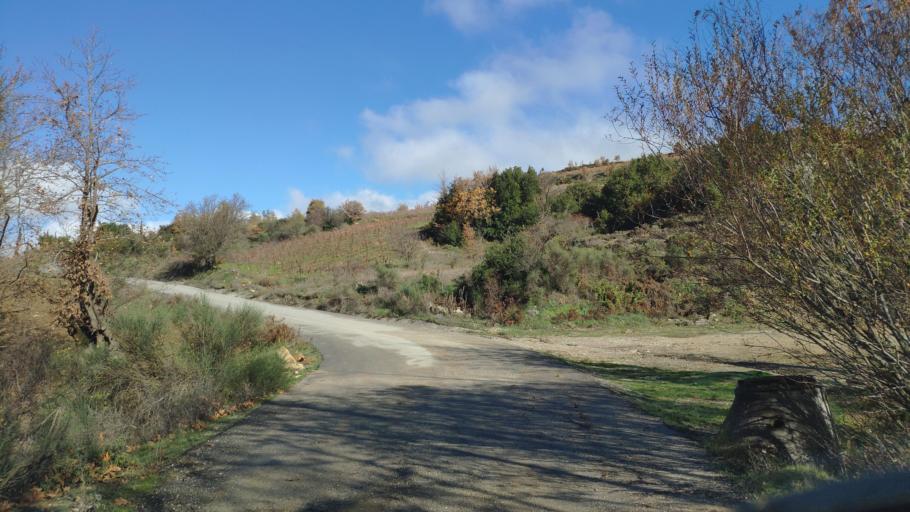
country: GR
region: West Greece
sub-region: Nomos Achaias
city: Aiyira
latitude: 38.0624
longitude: 22.4634
